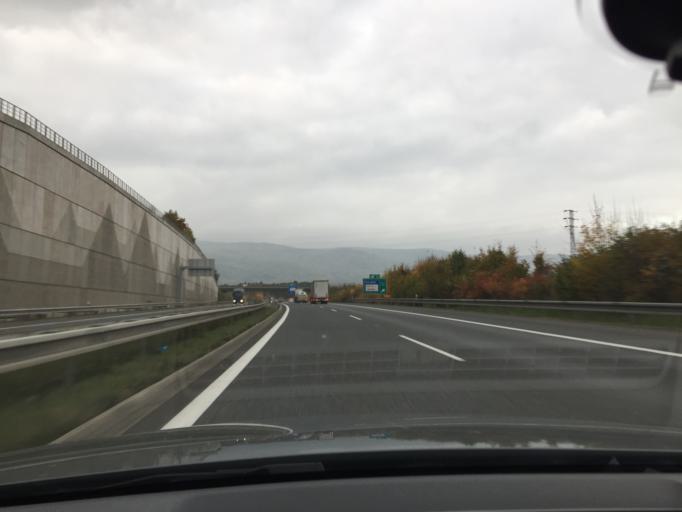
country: CZ
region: Ustecky
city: Chabarovice
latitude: 50.6823
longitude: 13.9583
